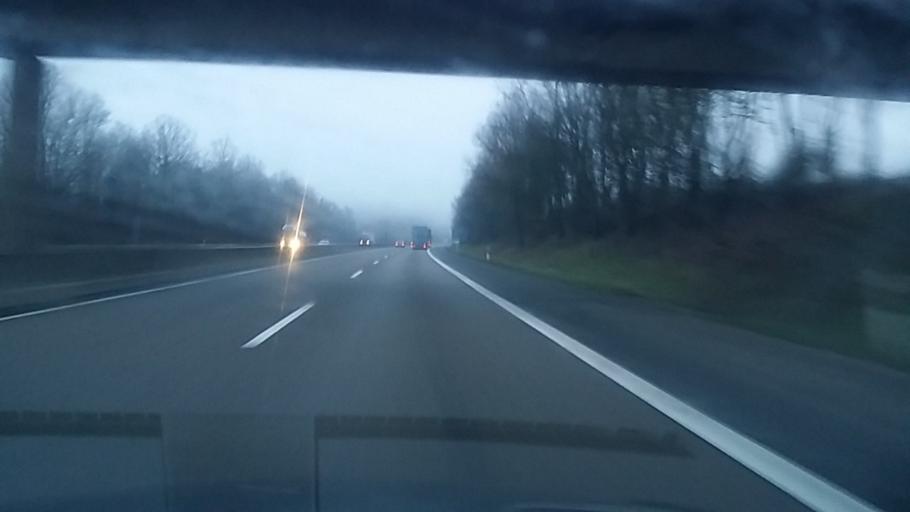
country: DE
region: Hesse
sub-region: Regierungsbezirk Kassel
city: Burghaun
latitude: 50.6671
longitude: 9.6768
